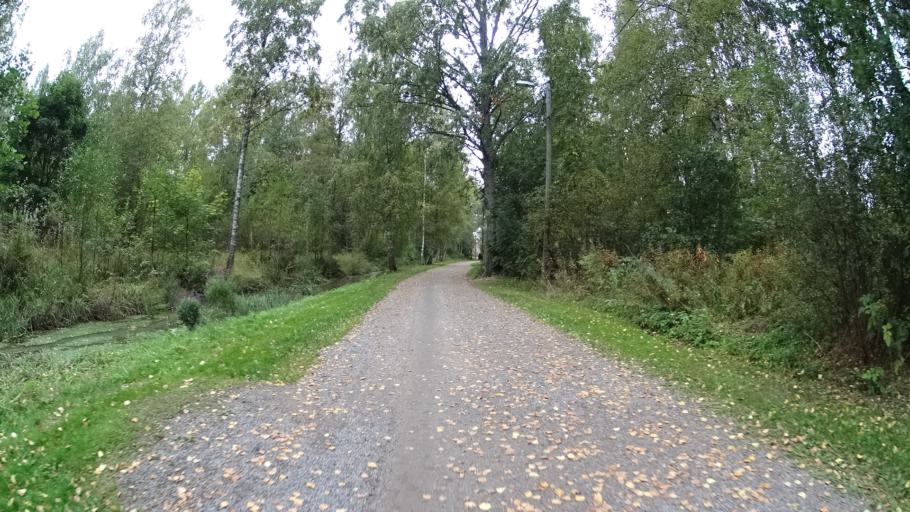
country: FI
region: Uusimaa
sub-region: Helsinki
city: Kauniainen
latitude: 60.2089
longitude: 24.7176
